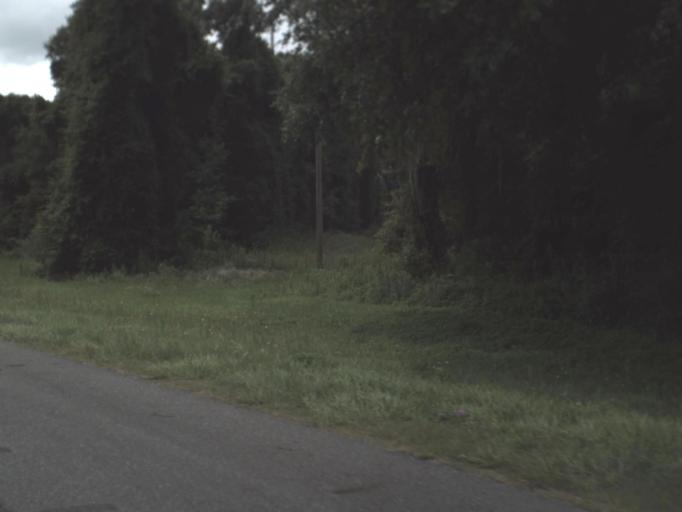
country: US
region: Florida
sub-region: Columbia County
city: Lake City
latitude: 30.0896
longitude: -82.6398
